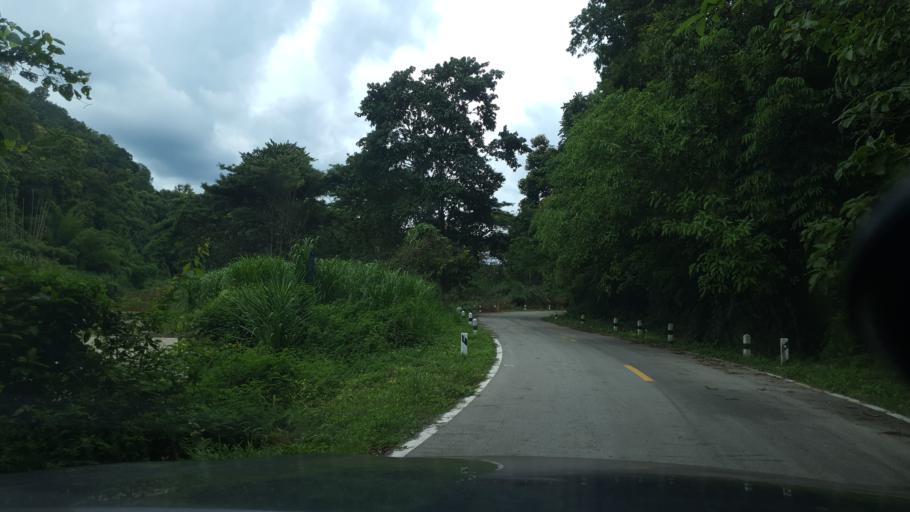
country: TH
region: Lamphun
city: Mae Tha
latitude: 18.4388
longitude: 99.2685
